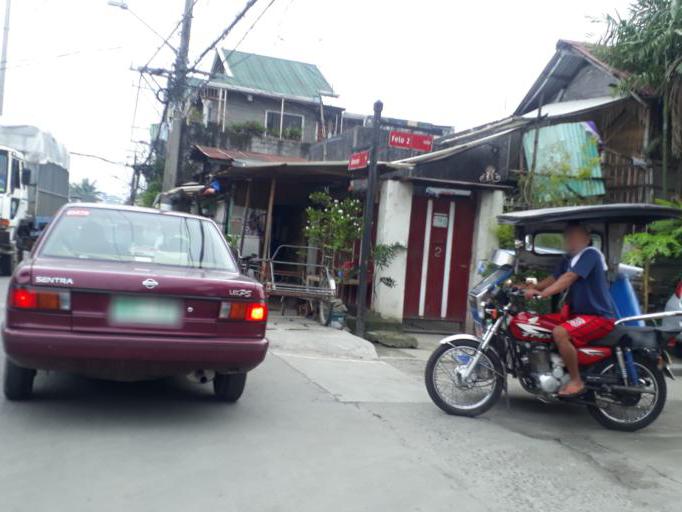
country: PH
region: Calabarzon
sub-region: Province of Rizal
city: Valenzuela
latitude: 14.7009
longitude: 120.9568
